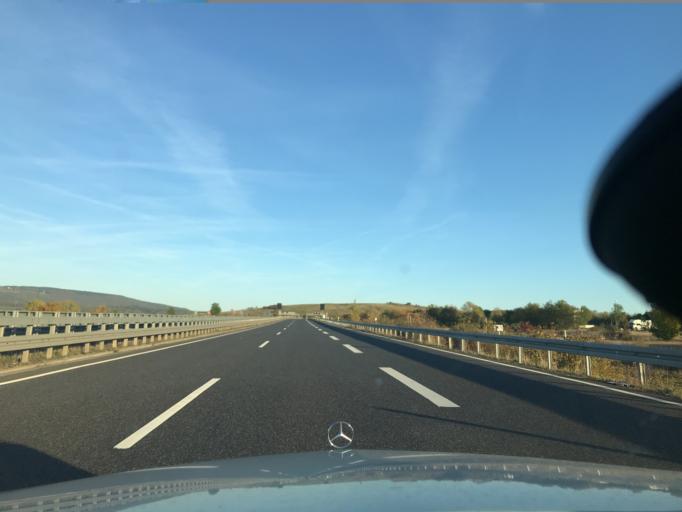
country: DE
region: Hesse
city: Hessisch Lichtenau
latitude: 51.2001
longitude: 9.7458
